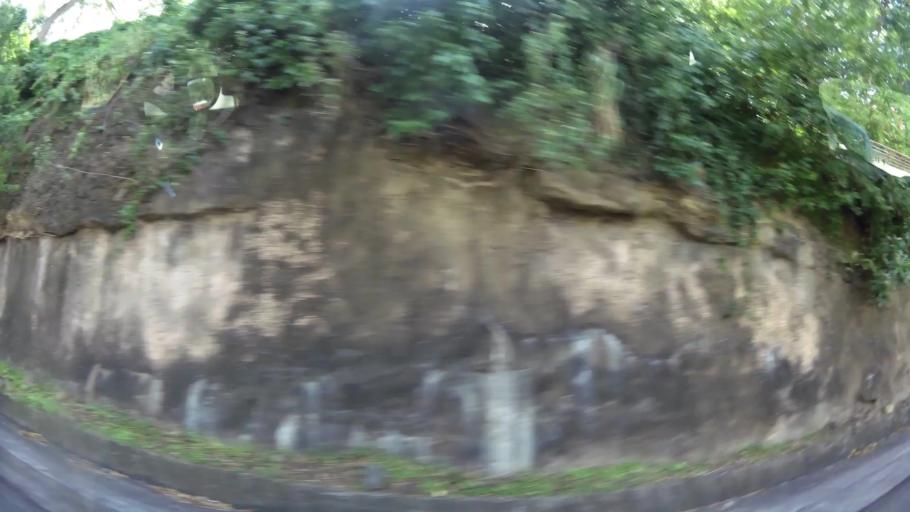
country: MQ
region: Martinique
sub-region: Martinique
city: Fort-de-France
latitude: 14.6169
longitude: -61.0999
